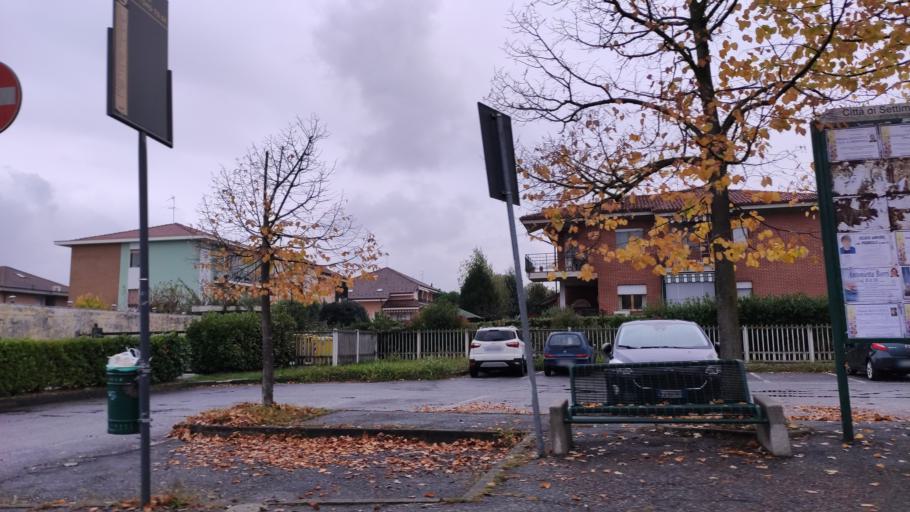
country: IT
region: Piedmont
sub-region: Provincia di Torino
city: Settimo Torinese
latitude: 45.1483
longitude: 7.7702
